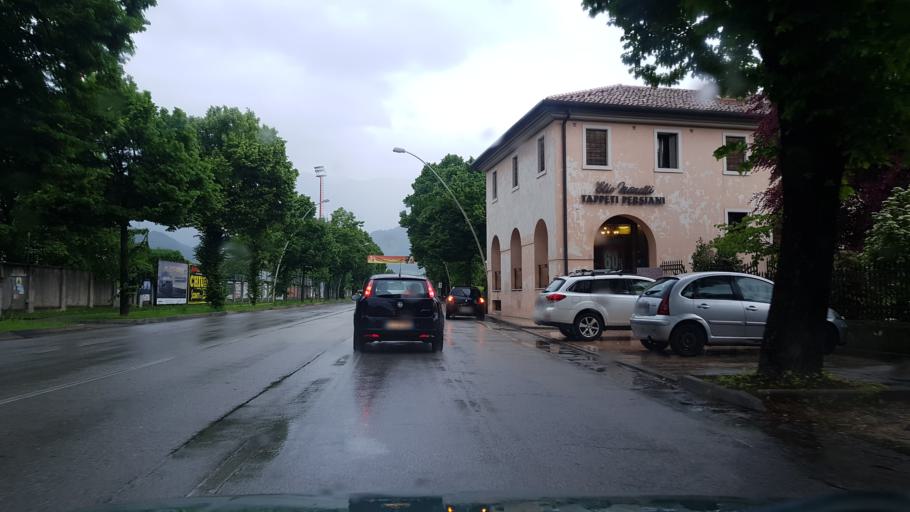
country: IT
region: Veneto
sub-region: Provincia di Treviso
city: Vittorio Veneto
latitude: 45.9771
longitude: 12.3070
